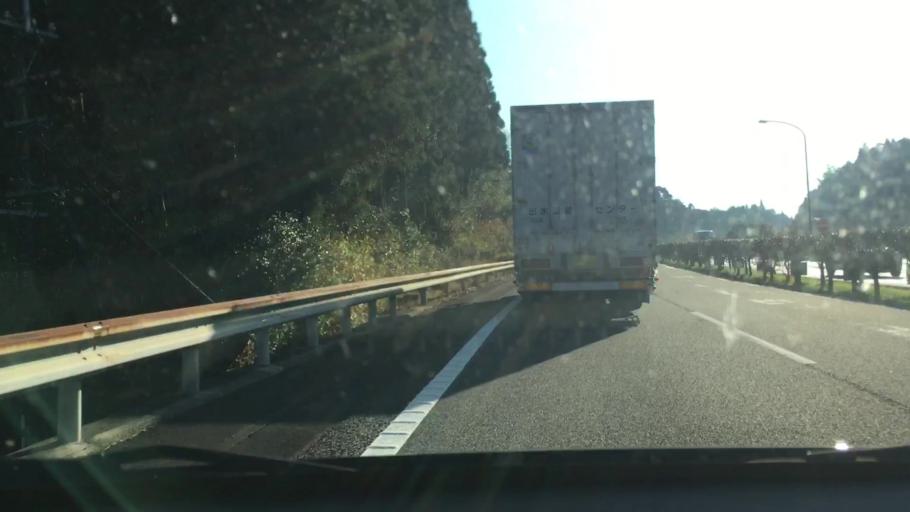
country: JP
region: Kagoshima
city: Kajiki
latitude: 31.8992
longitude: 130.7064
